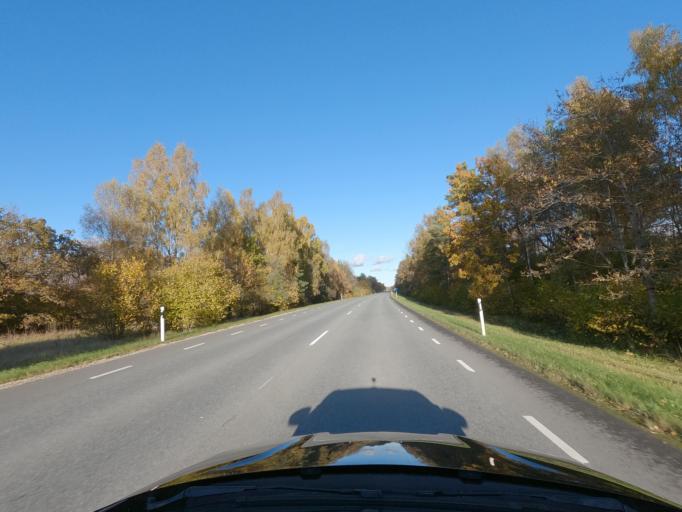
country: EE
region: Saare
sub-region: Kuressaare linn
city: Kuressaare
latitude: 58.3192
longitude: 22.6287
